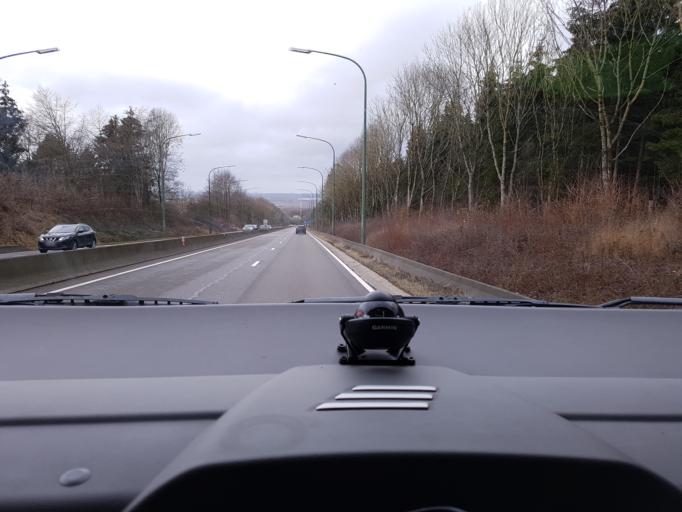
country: BE
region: Wallonia
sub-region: Province du Luxembourg
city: Marche-en-Famenne
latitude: 50.2137
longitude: 5.3581
